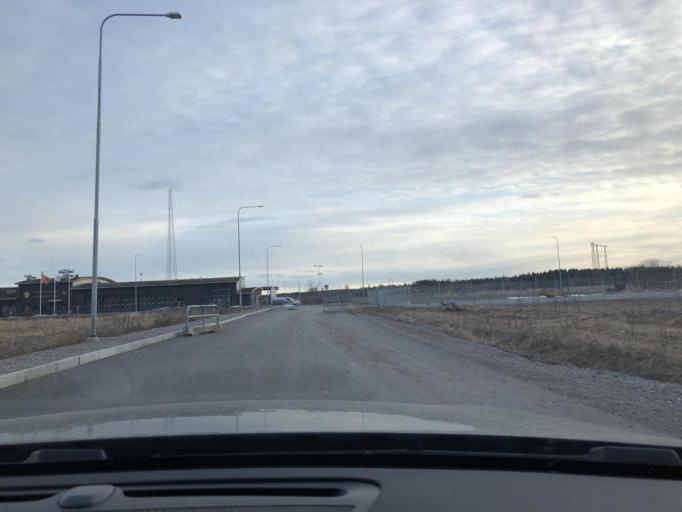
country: SE
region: Uppsala
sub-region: Tierps Kommun
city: Tierp
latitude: 60.3479
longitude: 17.4880
